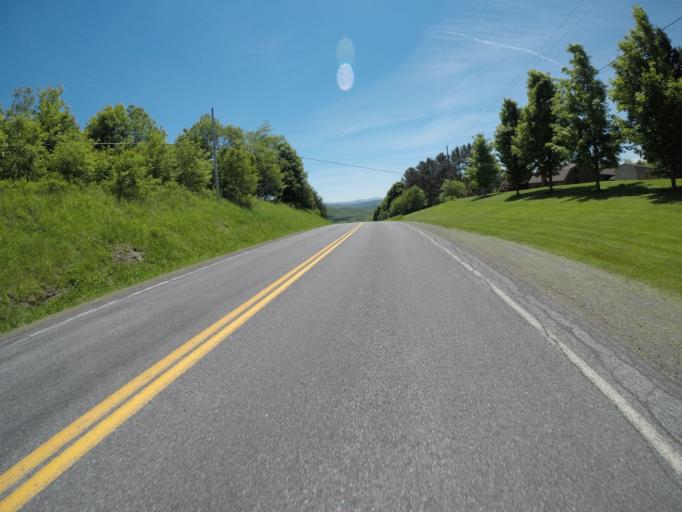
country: US
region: New York
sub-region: Delaware County
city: Delhi
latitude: 42.1991
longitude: -74.8454
